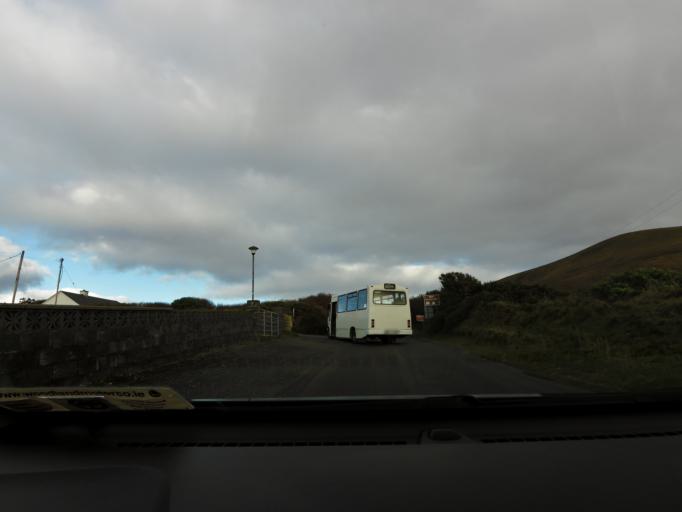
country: IE
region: Connaught
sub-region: Maigh Eo
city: Belmullet
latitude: 53.9273
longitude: -10.0180
